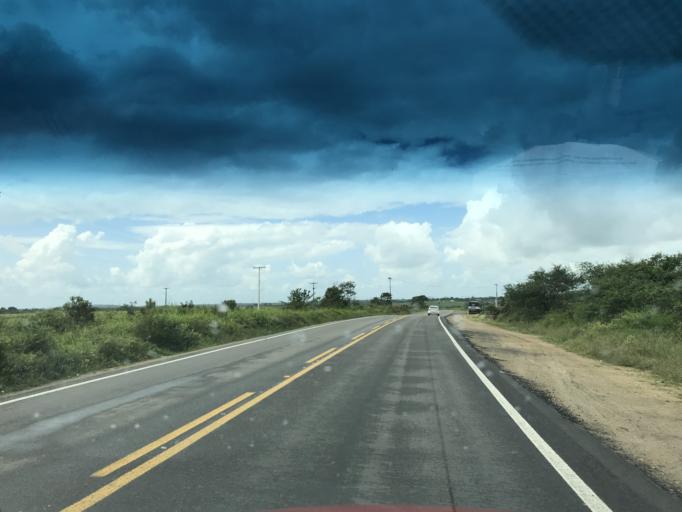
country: BR
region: Bahia
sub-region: Conceicao Do Almeida
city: Conceicao do Almeida
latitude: -12.6772
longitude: -39.2614
